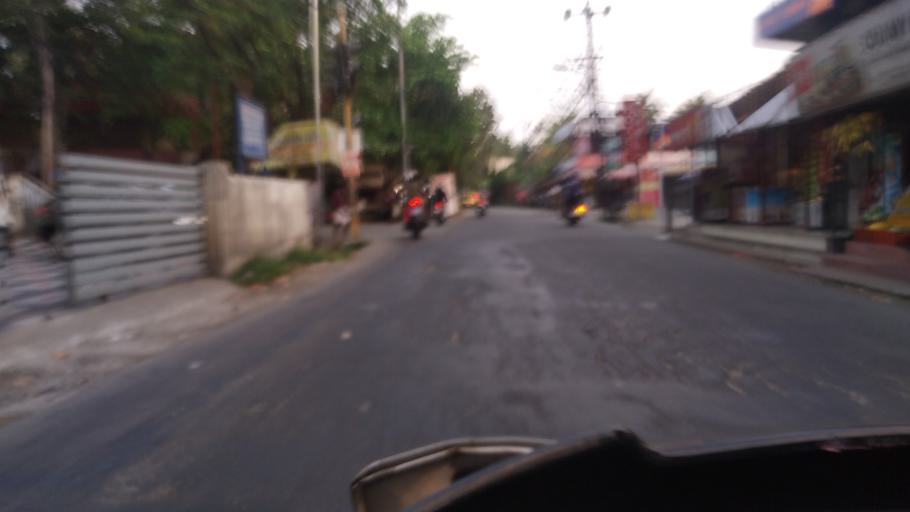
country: IN
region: Kerala
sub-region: Thrissur District
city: Kodungallur
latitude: 10.1823
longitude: 76.2047
